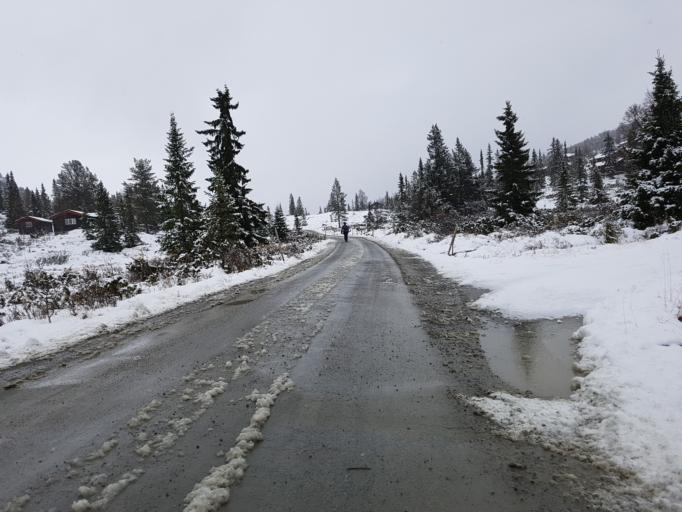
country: NO
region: Oppland
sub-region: Sel
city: Otta
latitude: 61.8063
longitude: 9.6881
